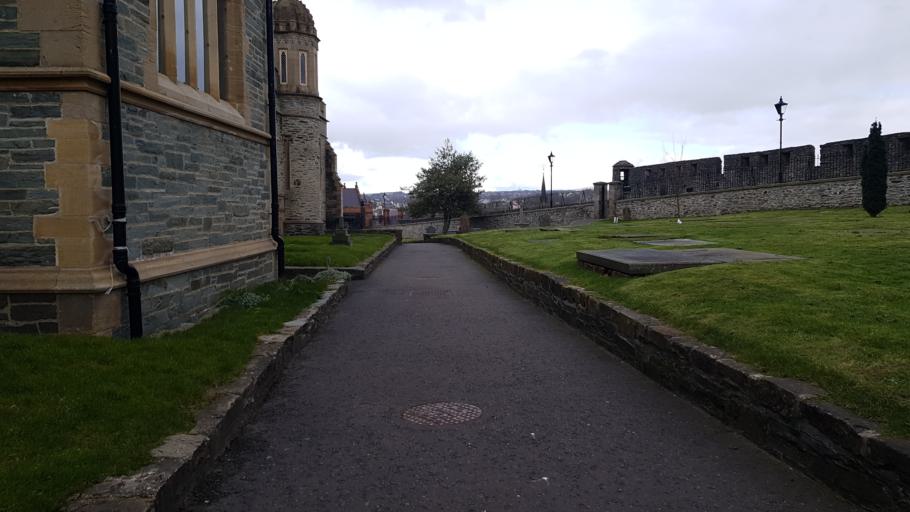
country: GB
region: Northern Ireland
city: Londonderry County Borough
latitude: 54.9938
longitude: -7.3233
